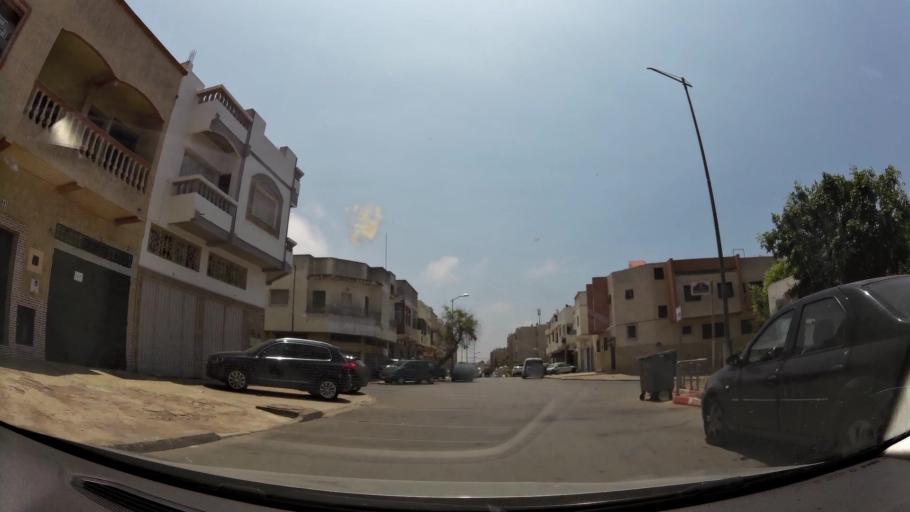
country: MA
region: Rabat-Sale-Zemmour-Zaer
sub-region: Skhirate-Temara
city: Temara
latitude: 33.9764
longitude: -6.8939
